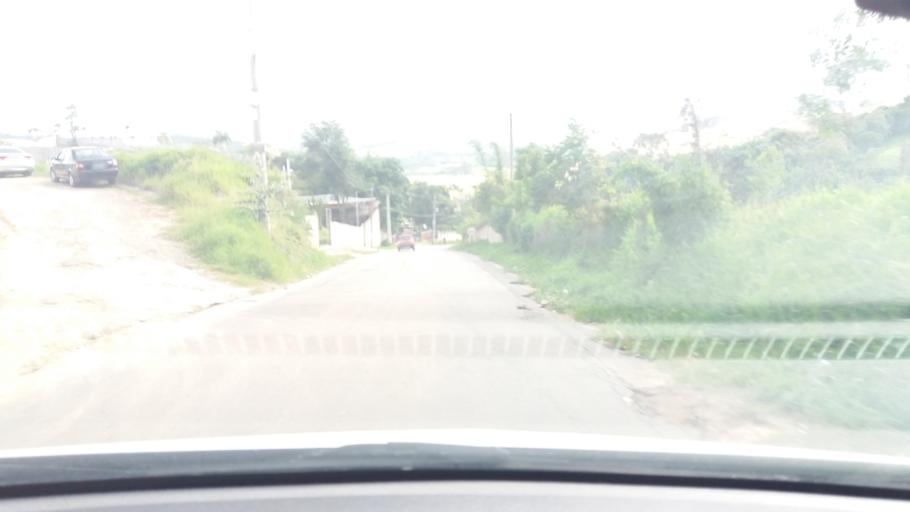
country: BR
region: Sao Paulo
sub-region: Bom Jesus Dos Perdoes
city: Bom Jesus dos Perdoes
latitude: -23.1488
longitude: -46.4696
